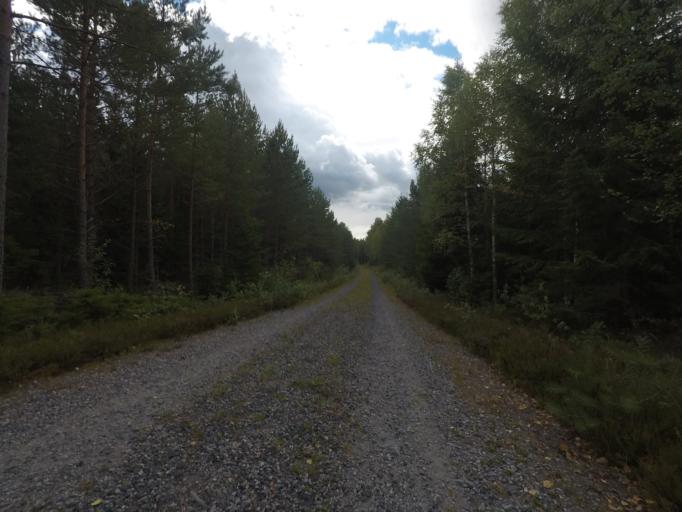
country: SE
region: Soedermanland
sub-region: Eskilstuna Kommun
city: Kvicksund
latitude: 59.4013
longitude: 16.2892
